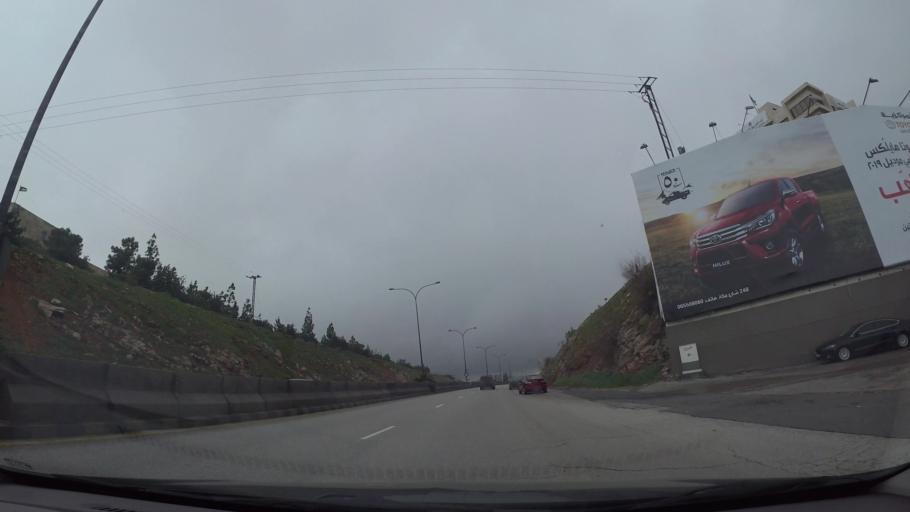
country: JO
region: Amman
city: Wadi as Sir
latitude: 31.9401
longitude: 35.8554
